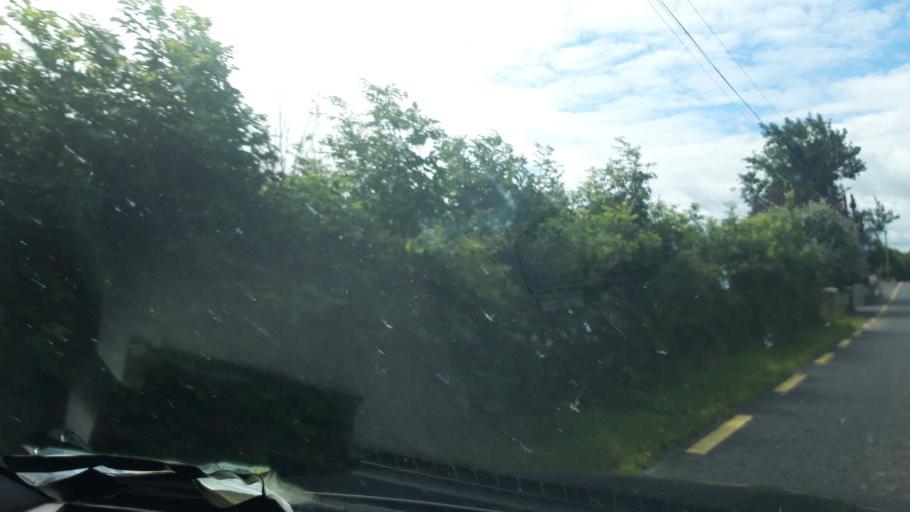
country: IE
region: Leinster
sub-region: Kilkenny
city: Callan
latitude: 52.5262
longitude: -7.4152
